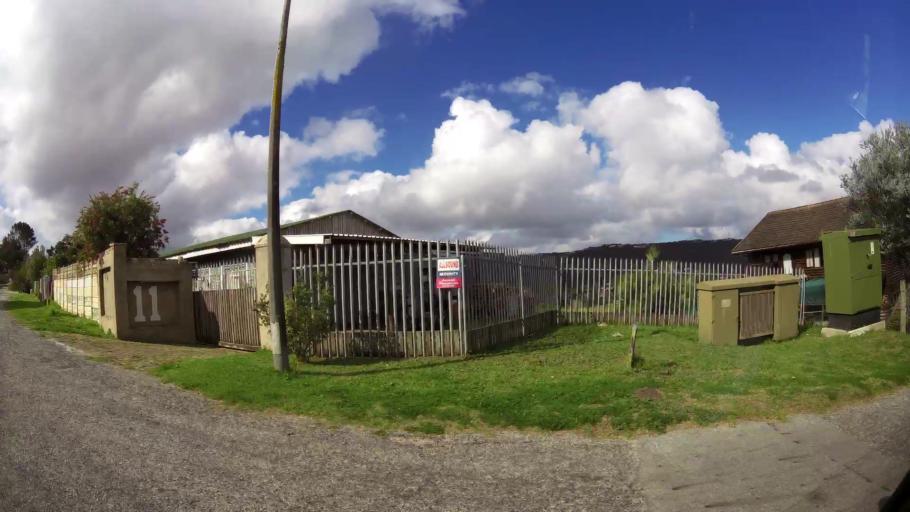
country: ZA
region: Western Cape
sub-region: Eden District Municipality
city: Knysna
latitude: -34.0531
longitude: 23.0847
